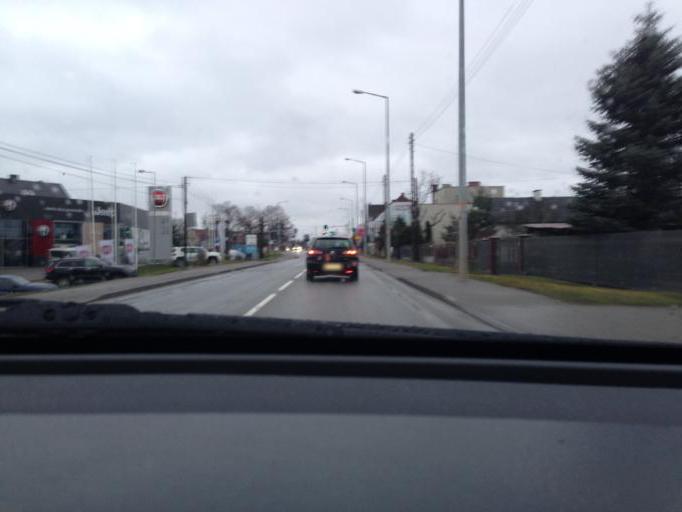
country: PL
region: Opole Voivodeship
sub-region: Powiat opolski
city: Opole
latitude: 50.6915
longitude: 17.9516
